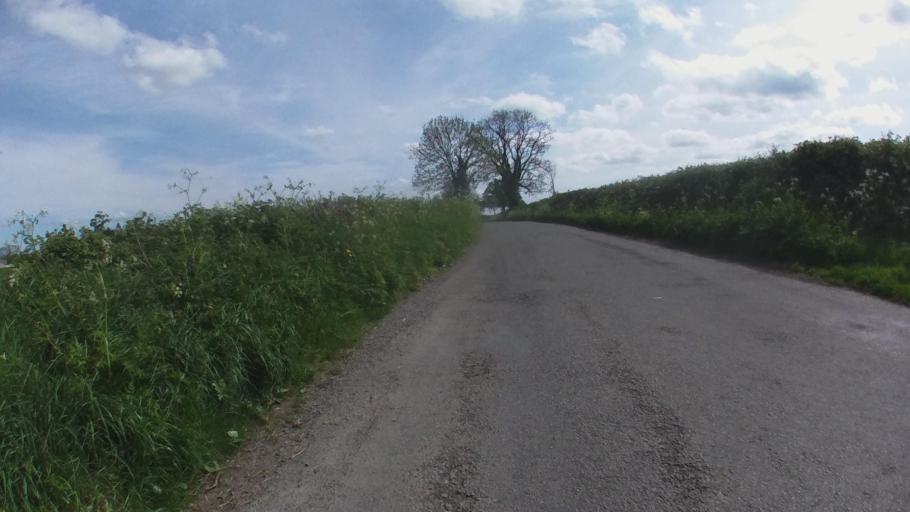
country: IE
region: Leinster
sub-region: County Carlow
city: Carlow
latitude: 52.8404
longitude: -6.9776
